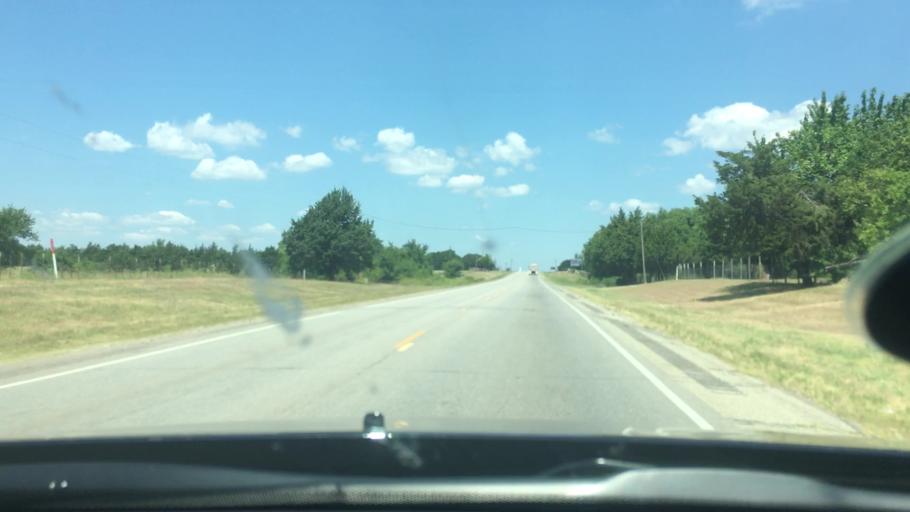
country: US
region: Oklahoma
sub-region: Marshall County
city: Oakland
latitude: 34.1243
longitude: -96.7845
